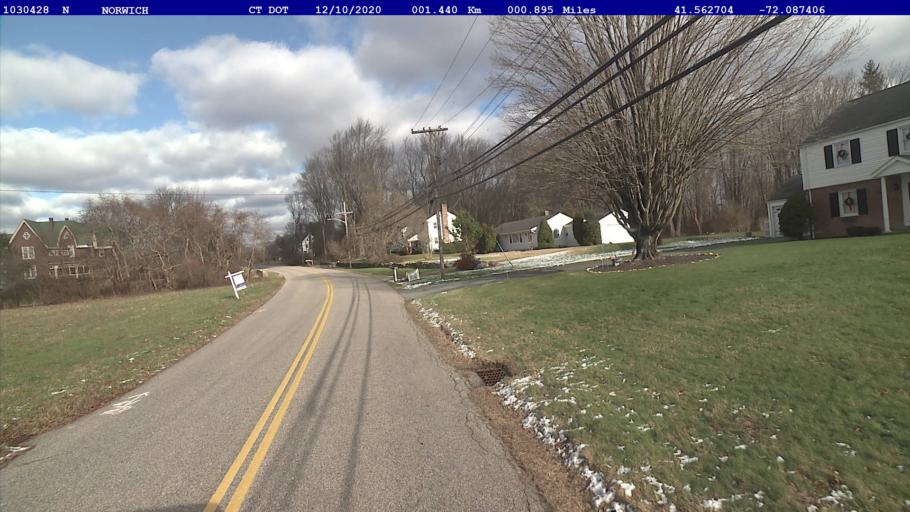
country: US
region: Connecticut
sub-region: New London County
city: Norwich
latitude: 41.5627
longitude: -72.0874
